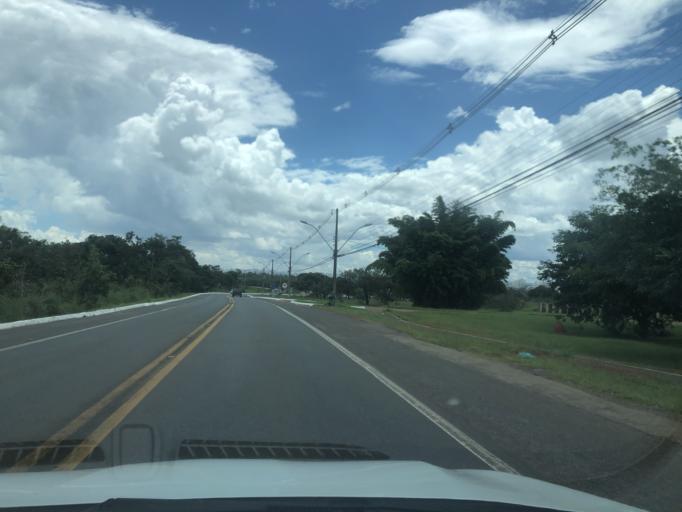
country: BR
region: Federal District
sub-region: Brasilia
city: Brasilia
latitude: -15.8839
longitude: -47.9566
